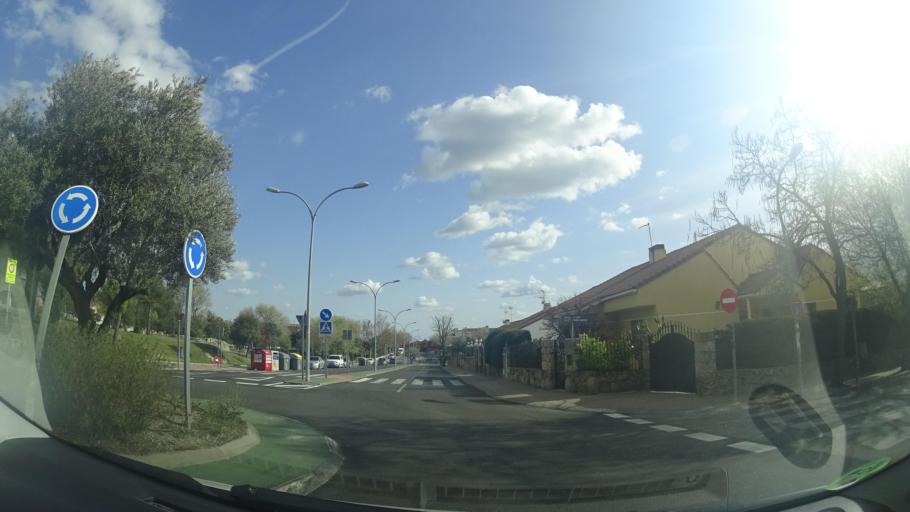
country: ES
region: Madrid
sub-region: Provincia de Madrid
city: Colmenar Viejo
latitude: 40.6591
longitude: -3.7765
